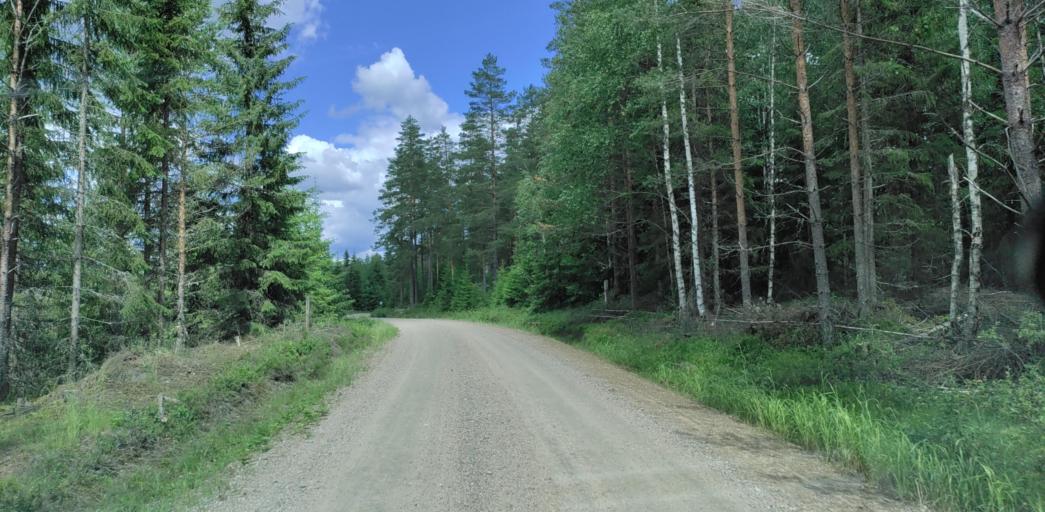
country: SE
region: Vaermland
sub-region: Hagfors Kommun
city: Ekshaerad
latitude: 60.0671
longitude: 13.2905
